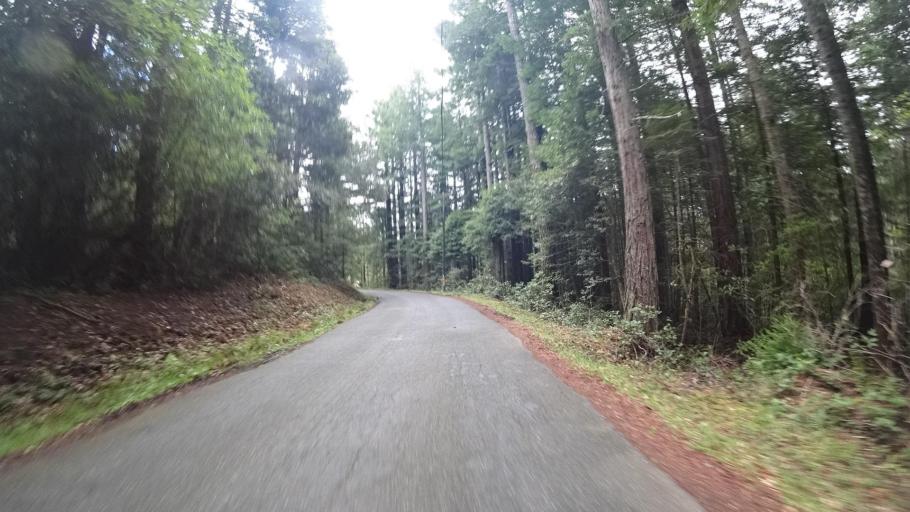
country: US
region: California
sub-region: Humboldt County
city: Blue Lake
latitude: 40.8198
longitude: -123.9979
